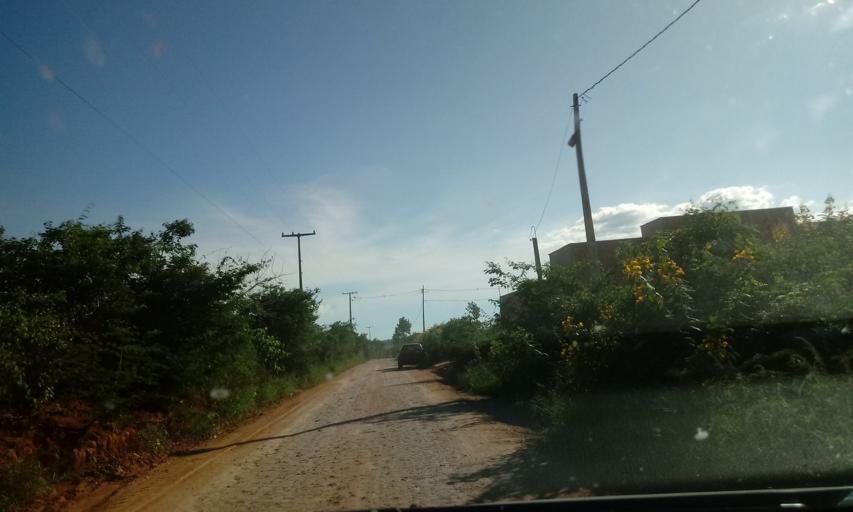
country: BR
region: Bahia
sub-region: Riacho De Santana
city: Riacho de Santana
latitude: -13.7843
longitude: -42.7246
